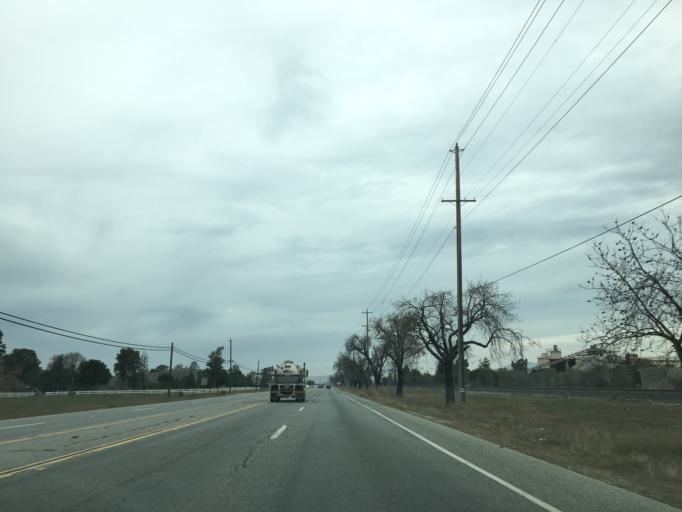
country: US
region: California
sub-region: Santa Clara County
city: San Martin
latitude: 37.0892
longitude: -121.6127
